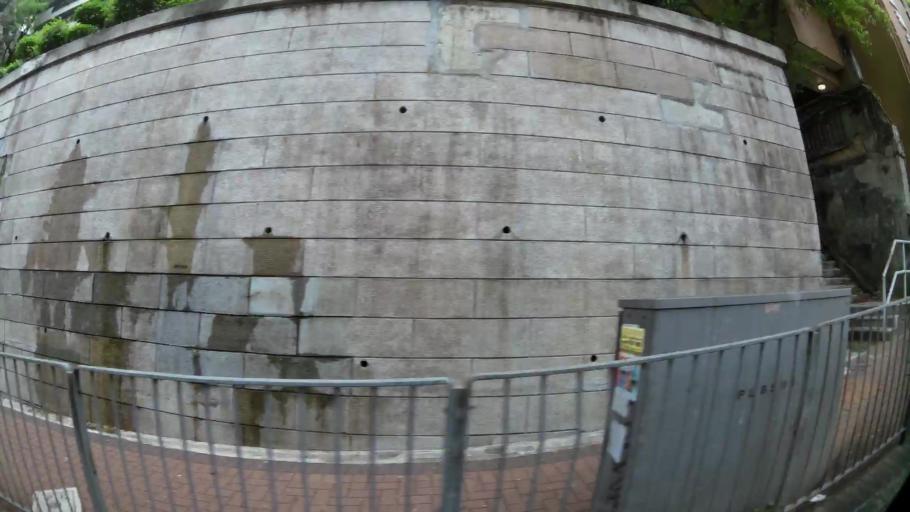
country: HK
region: Wanchai
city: Wan Chai
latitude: 22.2729
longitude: 114.1742
